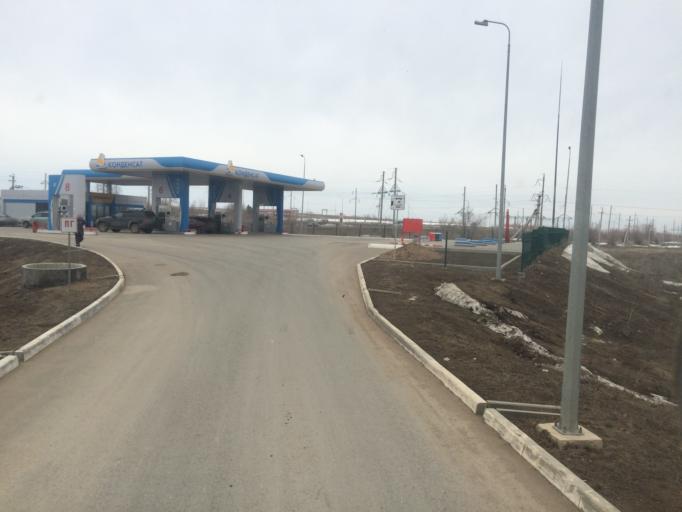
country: KZ
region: Batys Qazaqstan
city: Oral
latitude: 51.1894
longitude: 51.2655
